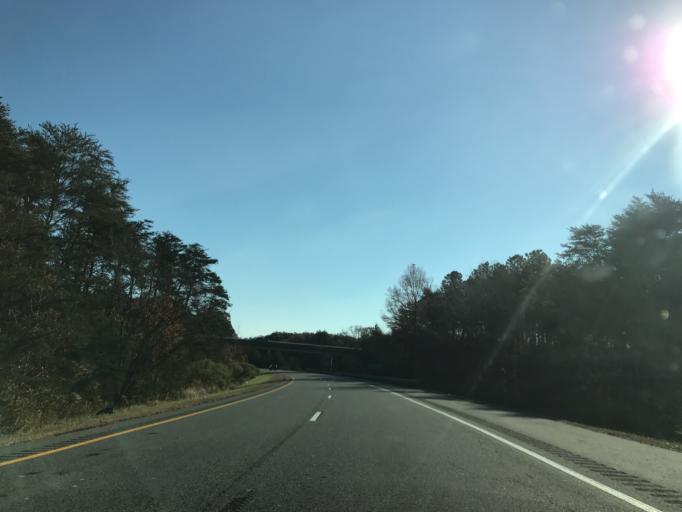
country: US
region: Maryland
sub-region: Anne Arundel County
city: Pasadena
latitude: 39.1223
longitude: -76.5771
